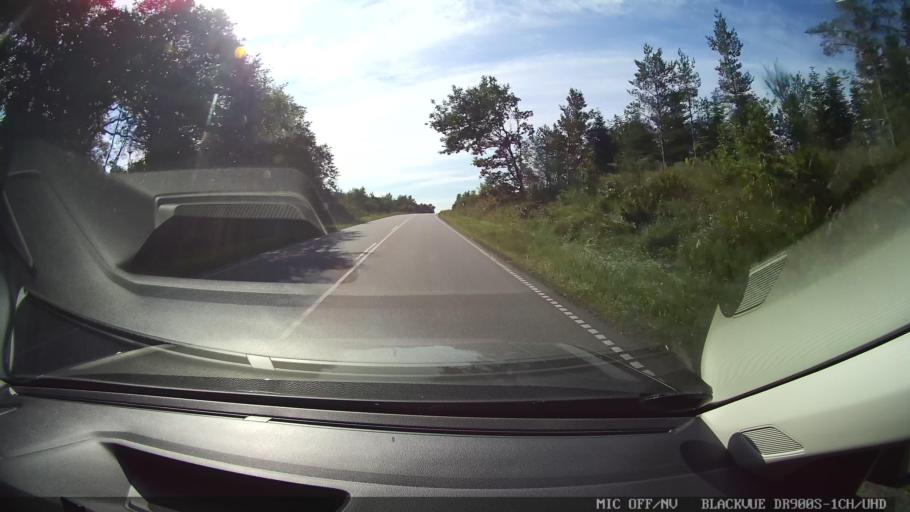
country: DK
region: North Denmark
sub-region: Mariagerfjord Kommune
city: Hadsund
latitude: 56.7548
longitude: 10.0711
